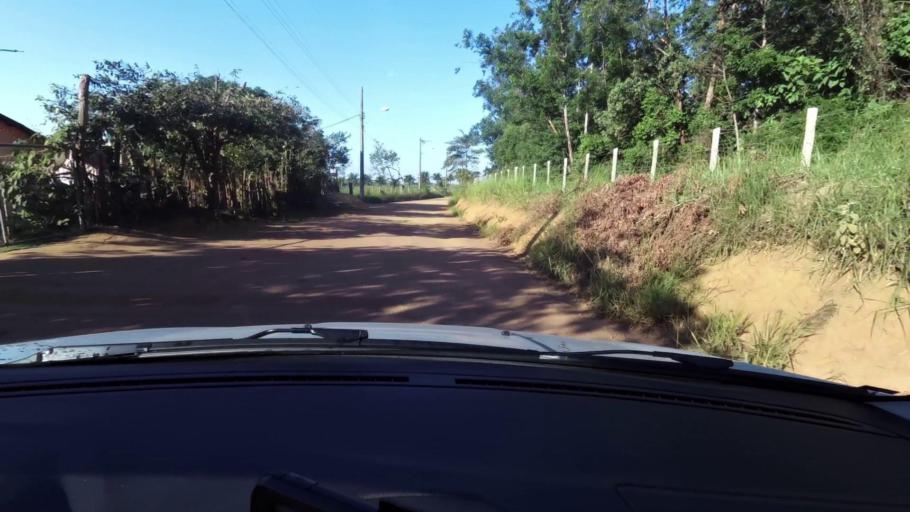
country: BR
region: Espirito Santo
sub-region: Guarapari
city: Guarapari
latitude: -20.7234
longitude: -40.5804
